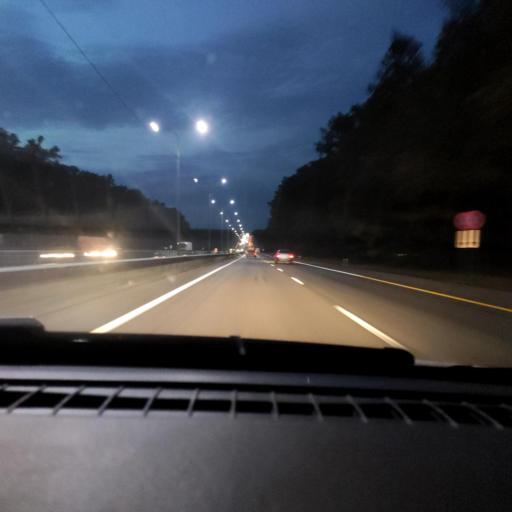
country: RU
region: Voronezj
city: Ramon'
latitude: 51.8625
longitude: 39.2159
